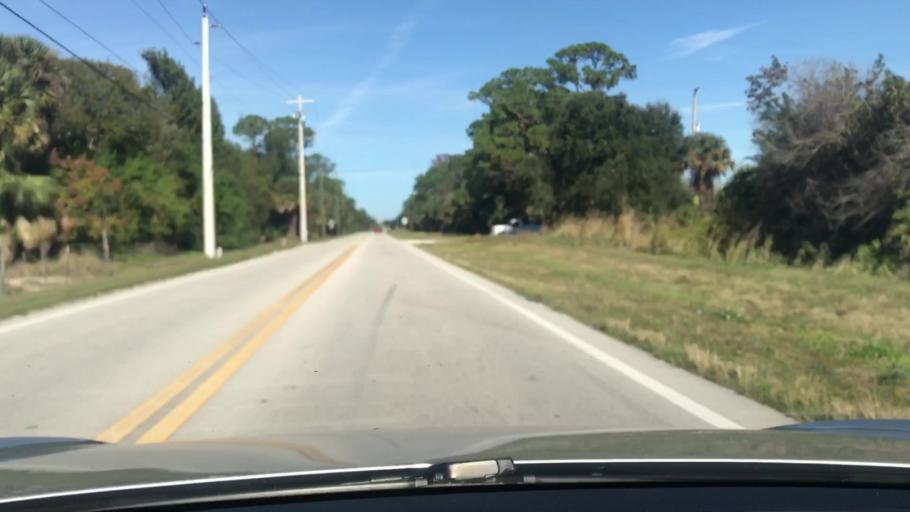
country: US
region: Florida
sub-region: Indian River County
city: Winter Beach
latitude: 27.7259
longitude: -80.4624
